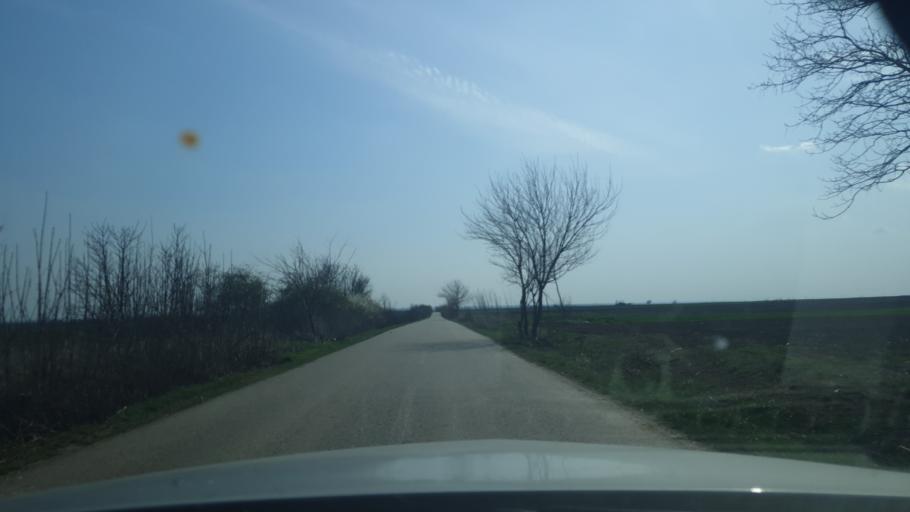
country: RS
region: Autonomna Pokrajina Vojvodina
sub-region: Sremski Okrug
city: Irig
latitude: 45.1083
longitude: 19.9311
